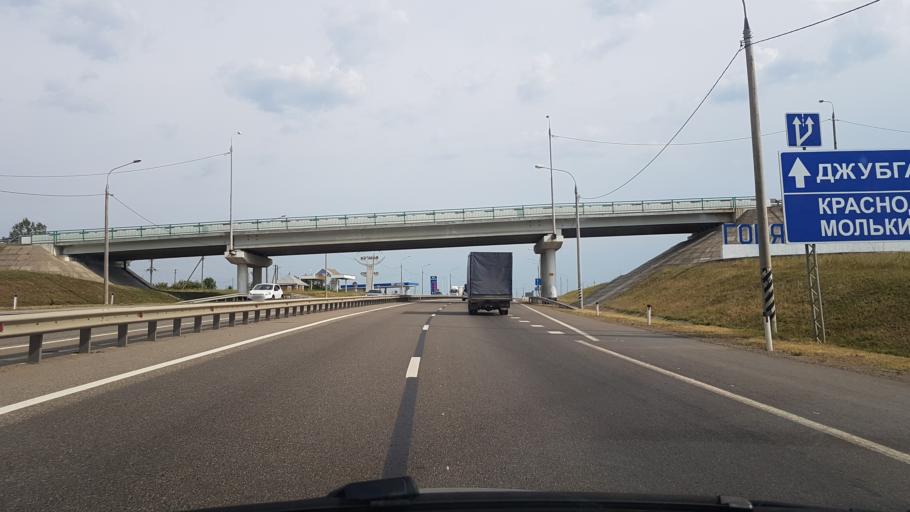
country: RU
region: Adygeya
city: Adygeysk
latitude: 44.8281
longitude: 39.2235
